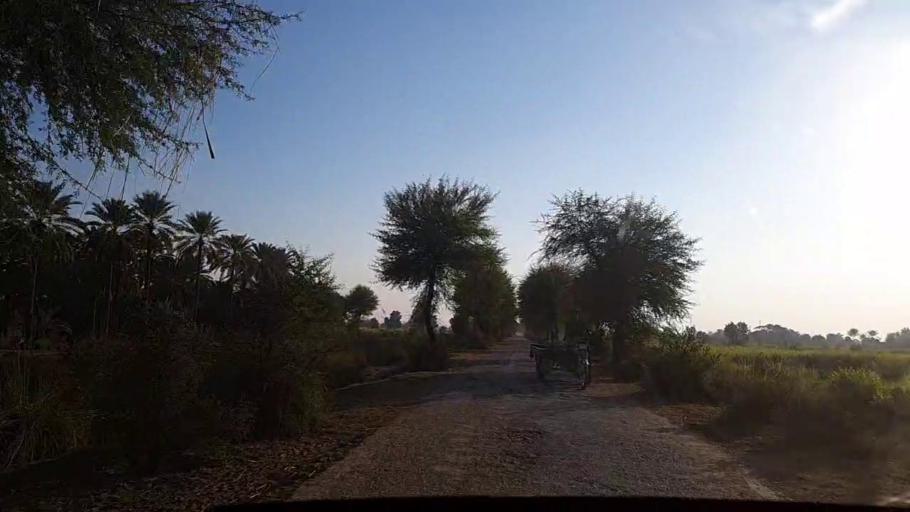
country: PK
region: Sindh
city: Sobhadero
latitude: 27.4031
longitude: 68.3906
